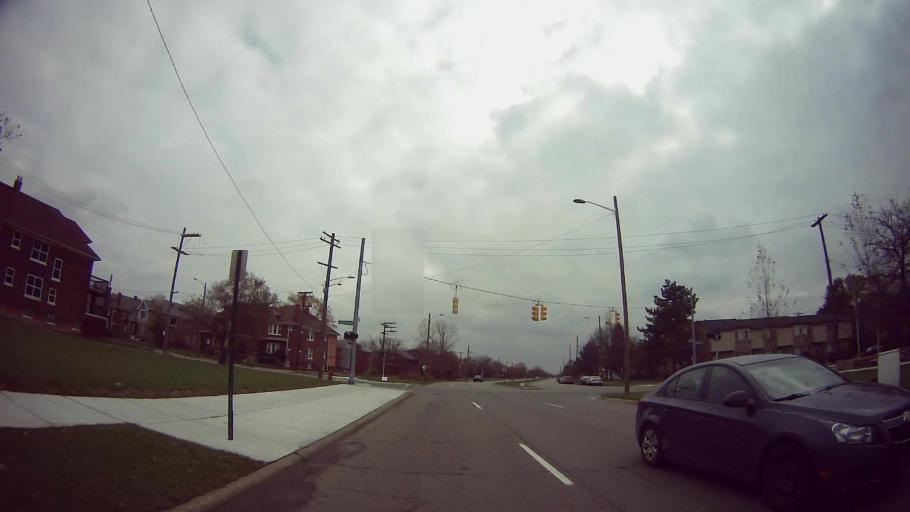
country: US
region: Michigan
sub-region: Wayne County
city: Highland Park
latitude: 42.3767
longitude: -83.0996
